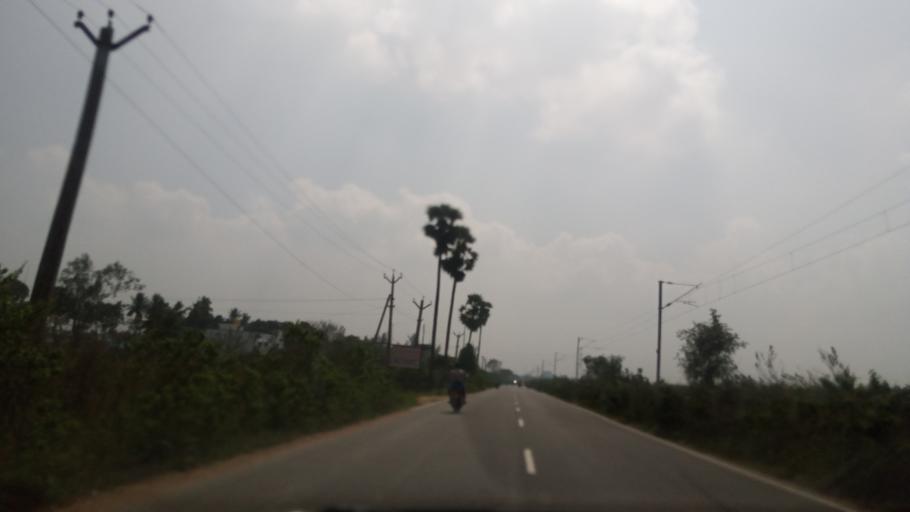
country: IN
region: Tamil Nadu
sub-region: Kancheepuram
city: Kanchipuram
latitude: 12.8935
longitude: 79.6859
